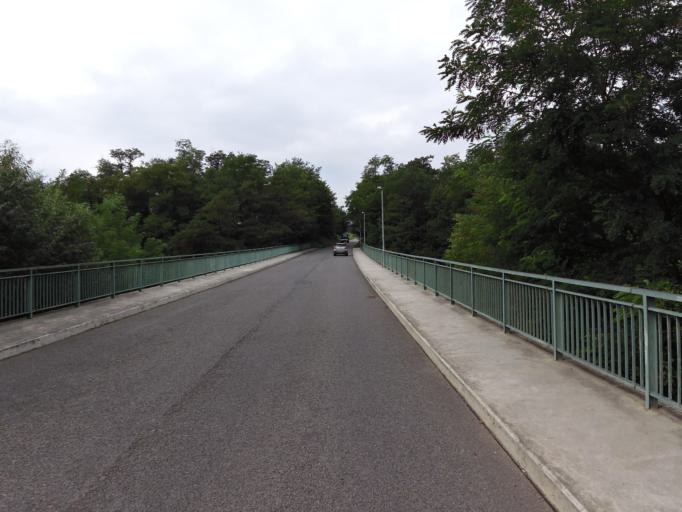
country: CZ
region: Central Bohemia
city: Tynec nad Sazavou
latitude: 49.8508
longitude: 14.5499
